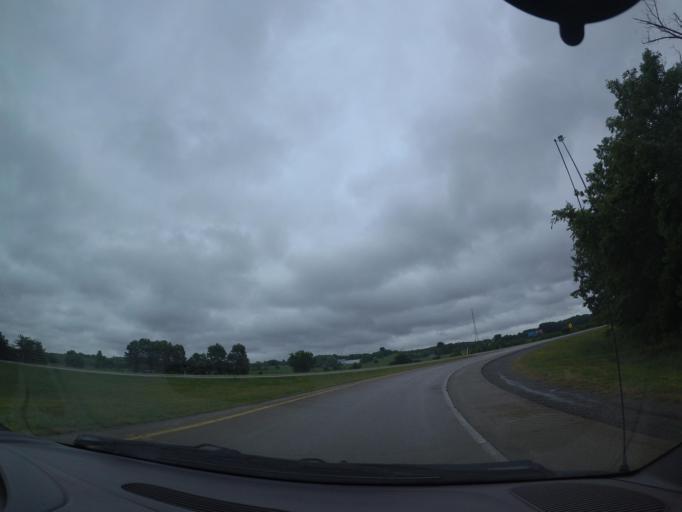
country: US
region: Ohio
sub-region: Ashtabula County
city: Conneaut
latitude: 41.9239
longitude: -80.5490
